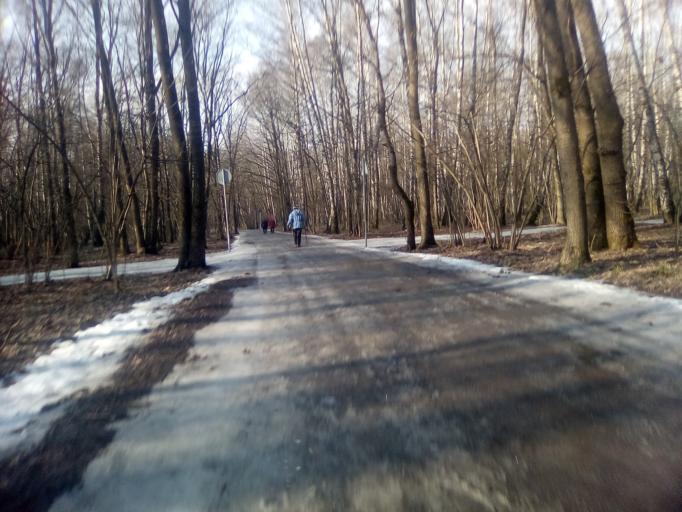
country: RU
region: Moscow
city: Tyoply Stan
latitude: 55.6370
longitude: 37.5021
